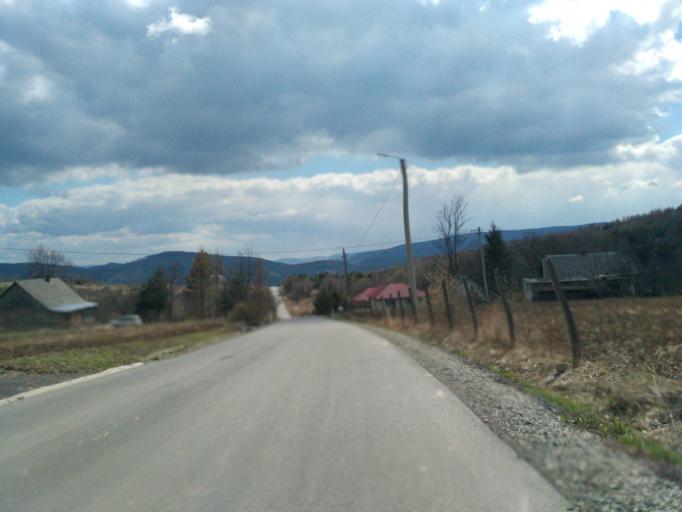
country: PL
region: Subcarpathian Voivodeship
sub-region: Powiat sanocki
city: Sanok
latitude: 49.6351
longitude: 22.2512
